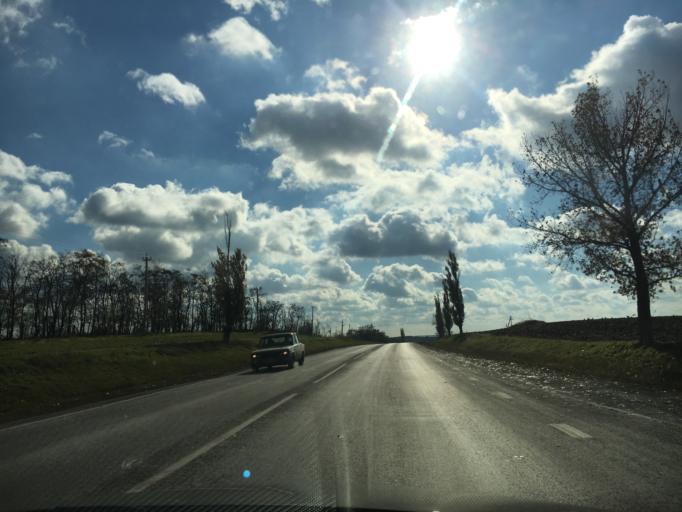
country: RU
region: Rostov
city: Matveyev Kurgan
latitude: 47.5612
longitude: 38.8888
